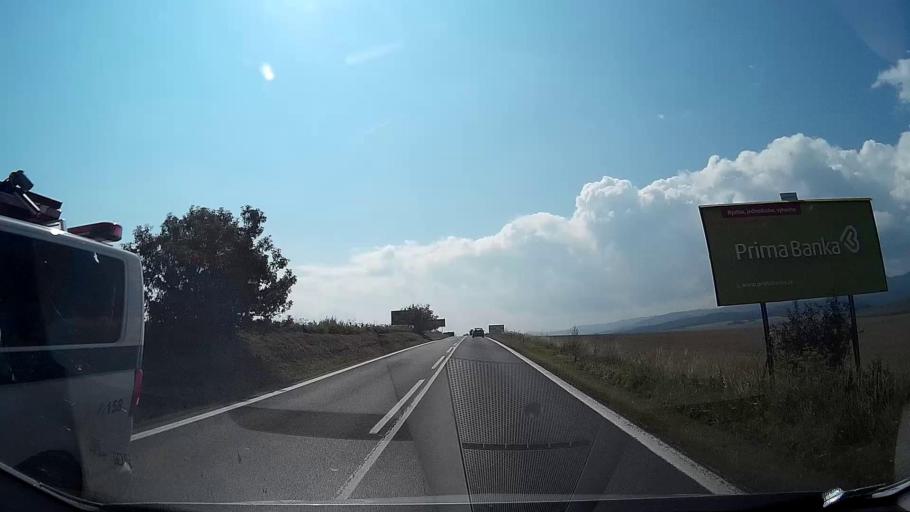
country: SK
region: Kosicky
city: Spisska Nova Ves
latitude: 48.9662
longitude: 20.4994
